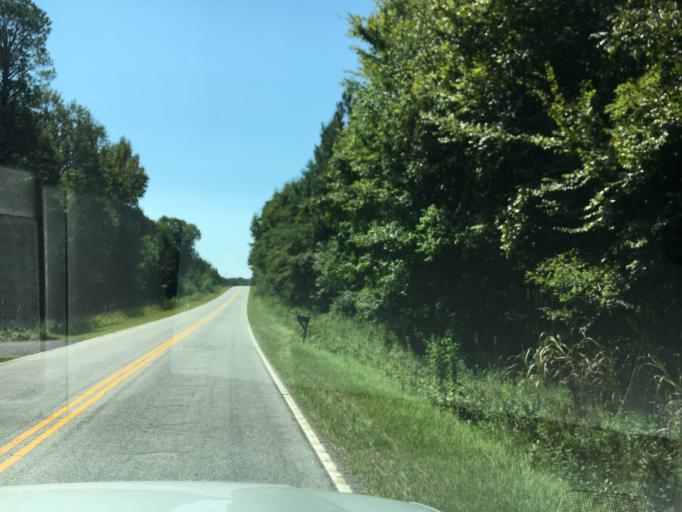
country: US
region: South Carolina
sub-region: Laurens County
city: Joanna
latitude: 34.3495
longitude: -81.8566
